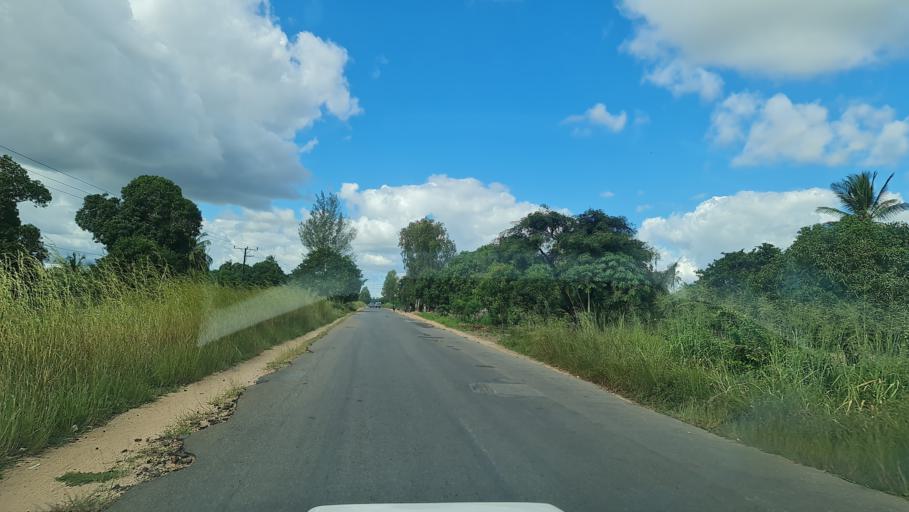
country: MZ
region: Zambezia
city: Quelimane
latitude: -17.5973
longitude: 36.7890
